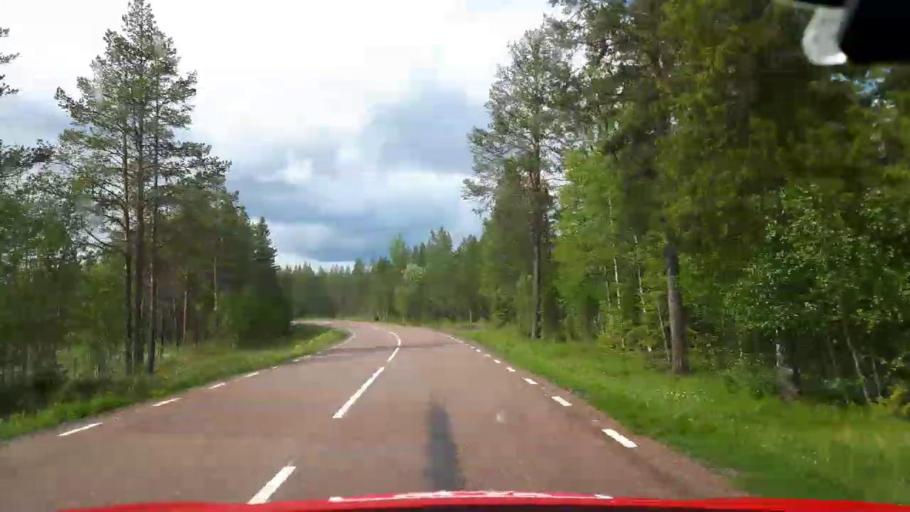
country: SE
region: Jaemtland
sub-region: Krokoms Kommun
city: Valla
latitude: 63.9666
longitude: 14.1702
